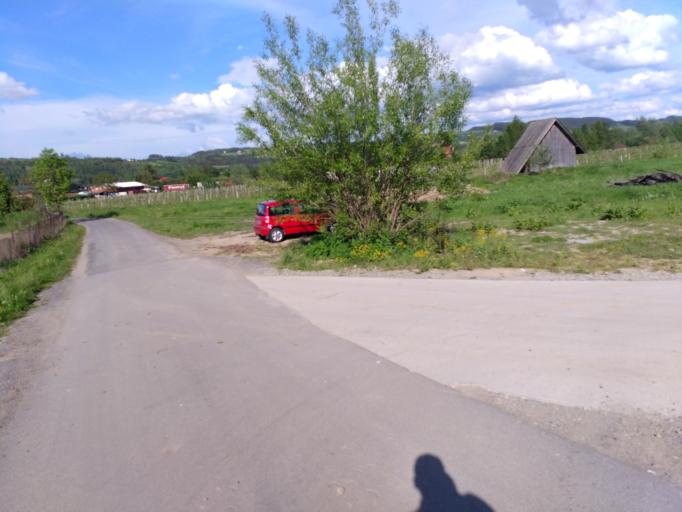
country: PL
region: Lesser Poland Voivodeship
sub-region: Powiat nowosadecki
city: Lacko
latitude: 49.5516
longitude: 20.4382
